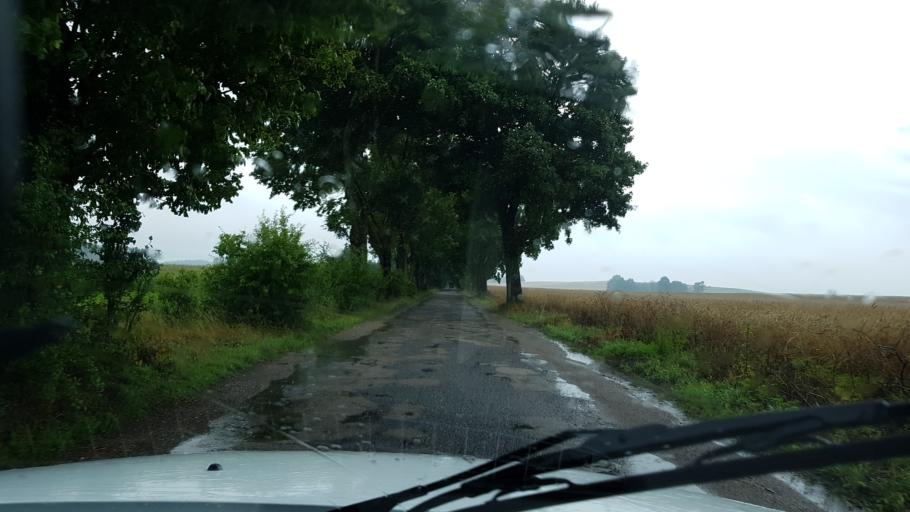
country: PL
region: West Pomeranian Voivodeship
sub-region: Powiat gryficki
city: Brojce
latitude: 53.9477
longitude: 15.4273
